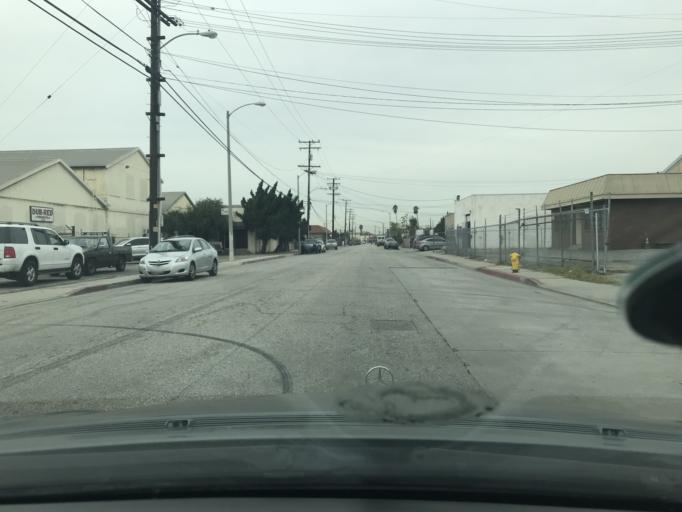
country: US
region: California
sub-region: Los Angeles County
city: Cudahy
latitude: 33.9581
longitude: -118.1811
